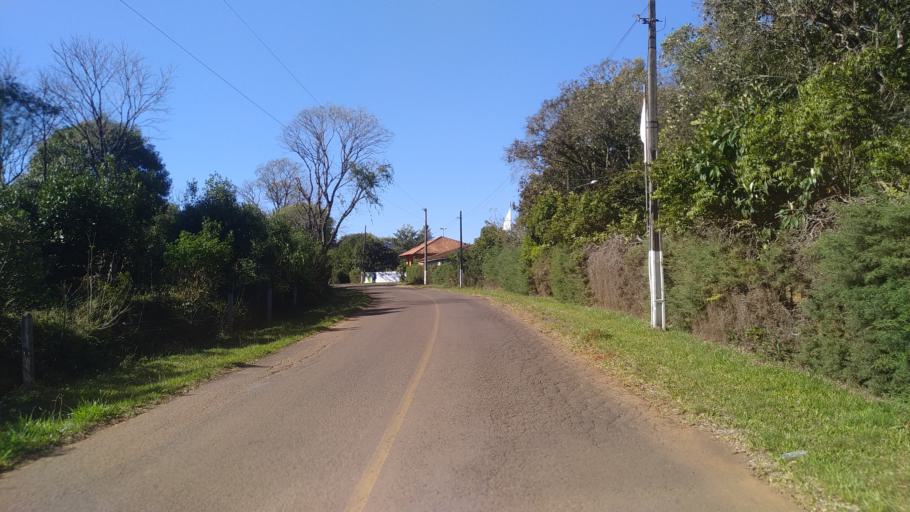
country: BR
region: Santa Catarina
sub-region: Chapeco
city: Chapeco
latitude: -27.1496
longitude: -52.6175
